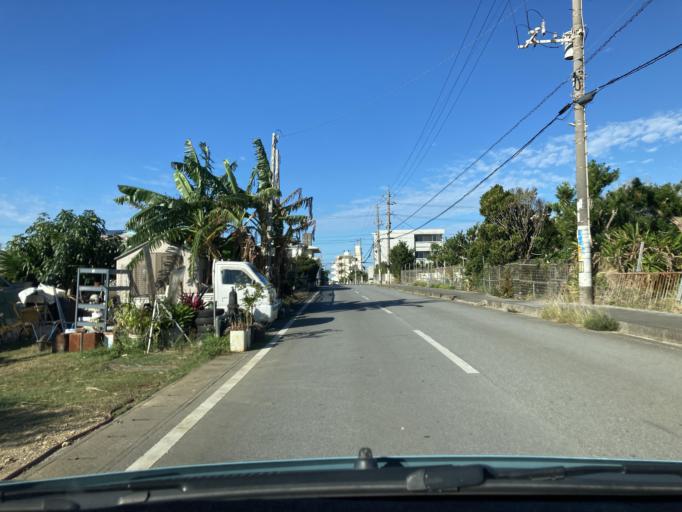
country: JP
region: Okinawa
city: Chatan
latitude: 26.3706
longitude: 127.7395
